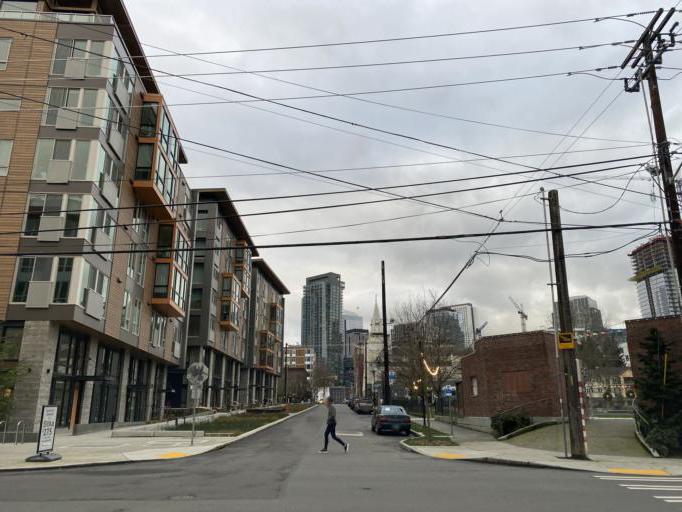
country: US
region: Washington
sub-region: King County
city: Seattle
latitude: 47.6221
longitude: -122.3318
